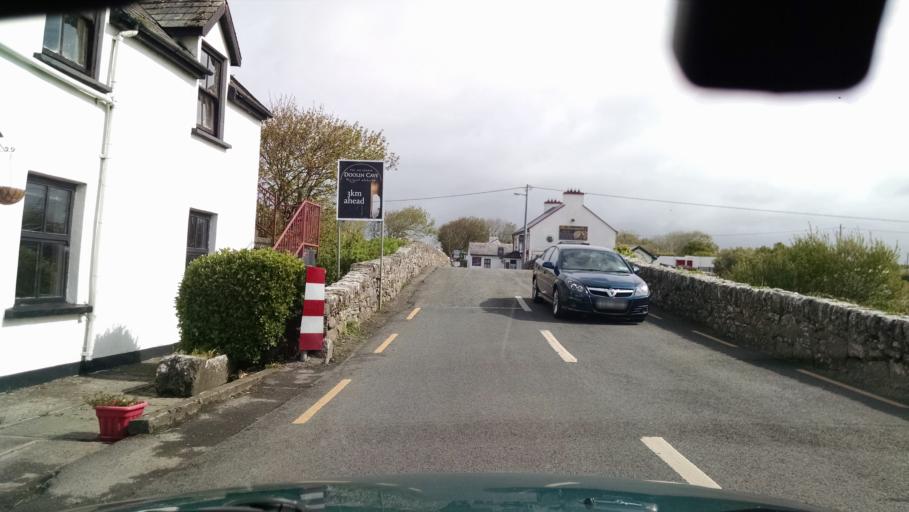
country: IE
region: Connaught
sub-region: County Galway
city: Bearna
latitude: 53.0184
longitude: -9.3720
